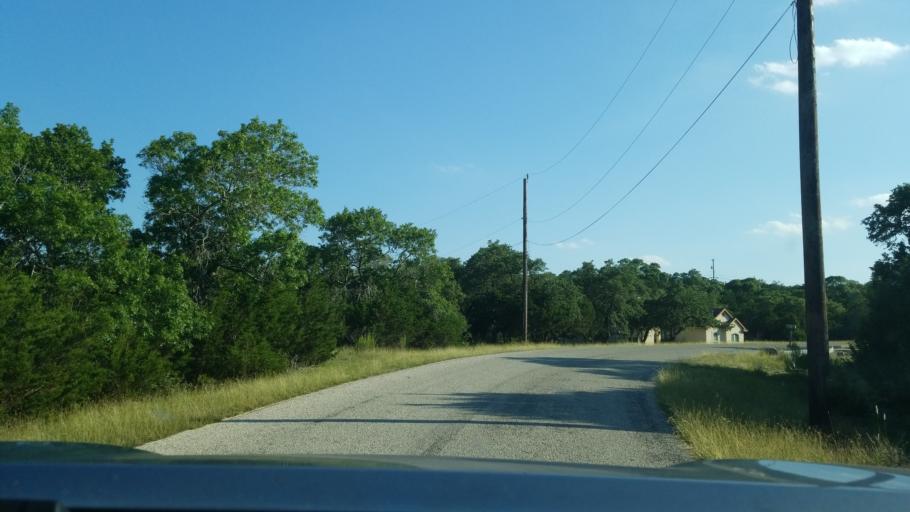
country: US
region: Texas
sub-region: Comal County
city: Bulverde
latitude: 29.7775
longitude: -98.4369
